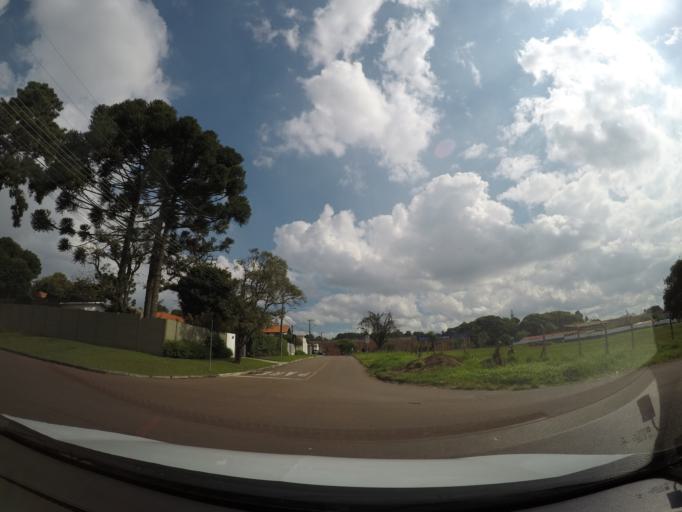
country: BR
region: Parana
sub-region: Curitiba
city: Curitiba
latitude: -25.4861
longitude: -49.2633
